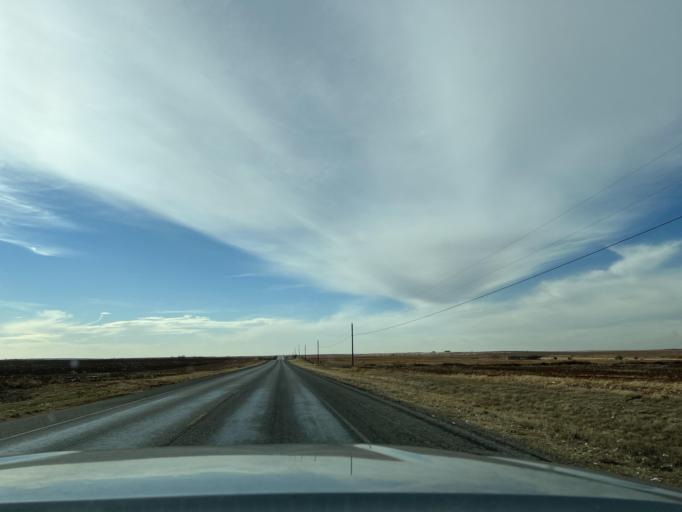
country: US
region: Texas
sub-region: Fisher County
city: Roby
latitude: 32.7414
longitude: -100.4628
